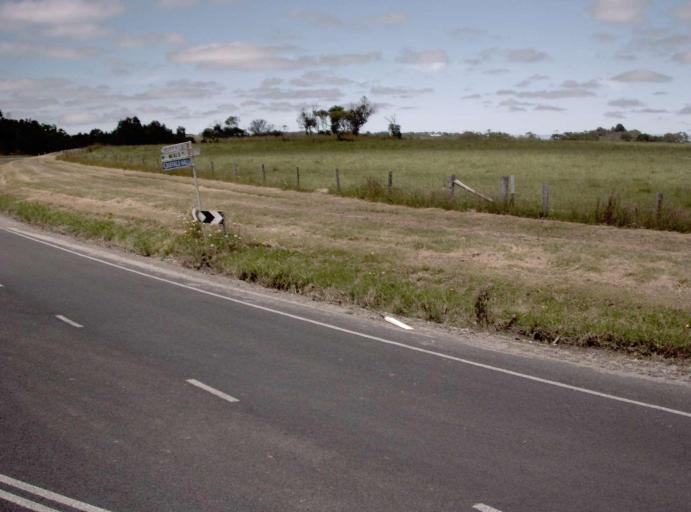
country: AU
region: Victoria
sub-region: Bass Coast
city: North Wonthaggi
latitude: -38.6500
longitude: 146.0185
